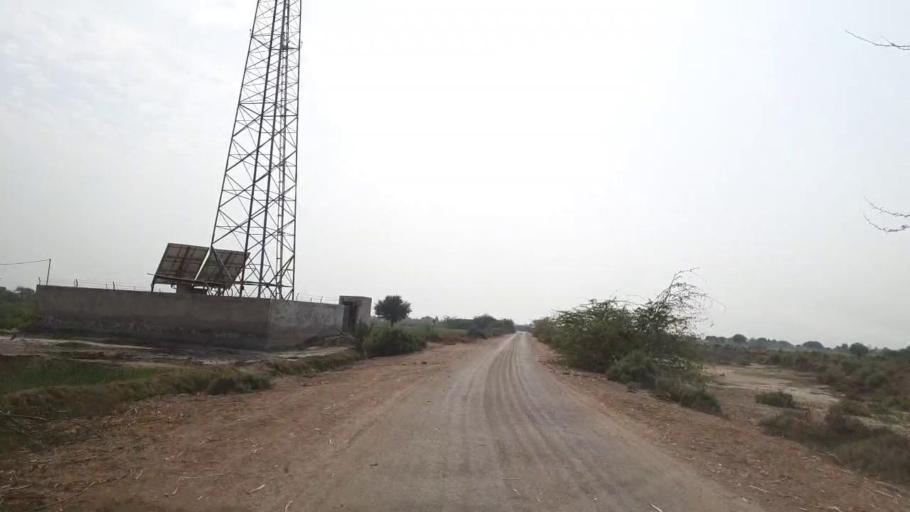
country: PK
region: Sindh
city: Mirpur Khas
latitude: 25.5407
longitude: 69.1608
